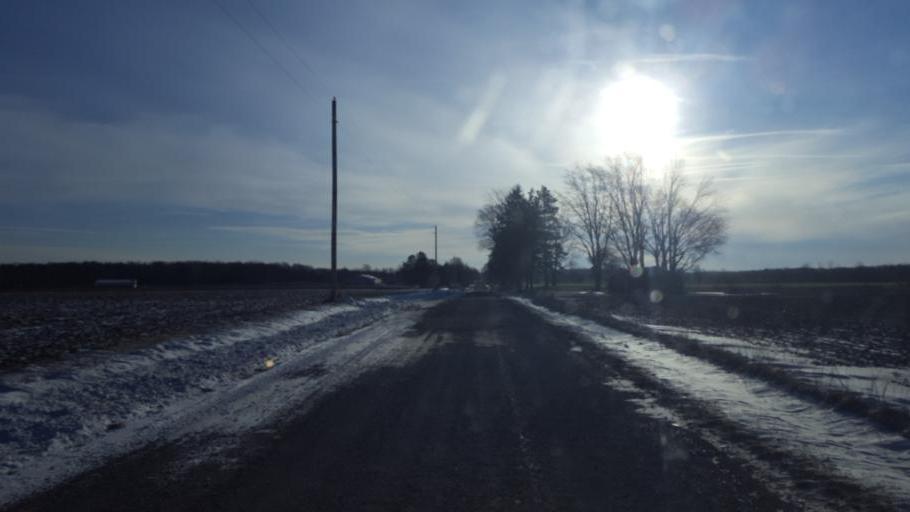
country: US
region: Ohio
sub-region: Morrow County
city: Mount Gilead
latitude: 40.6011
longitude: -82.8846
